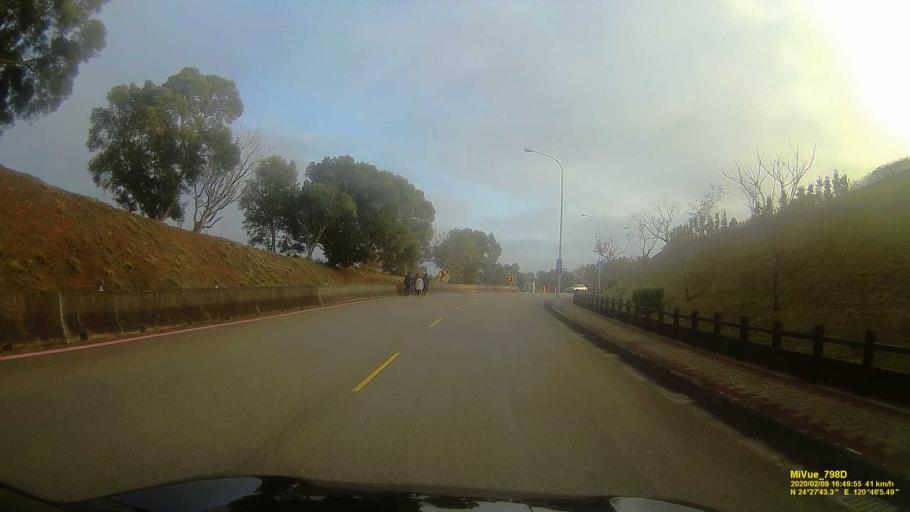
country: TW
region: Taiwan
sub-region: Miaoli
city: Miaoli
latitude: 24.4619
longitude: 120.7682
